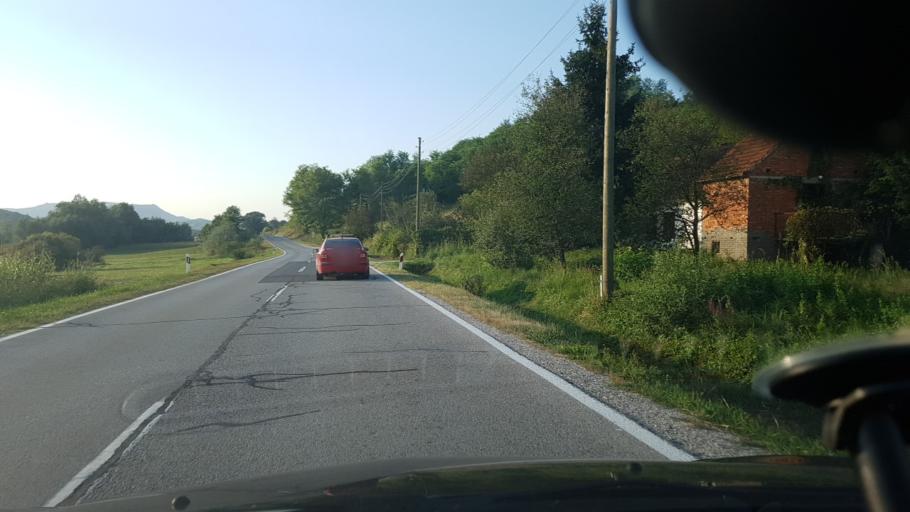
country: HR
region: Krapinsko-Zagorska
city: Pregrada
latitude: 46.1305
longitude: 15.7992
